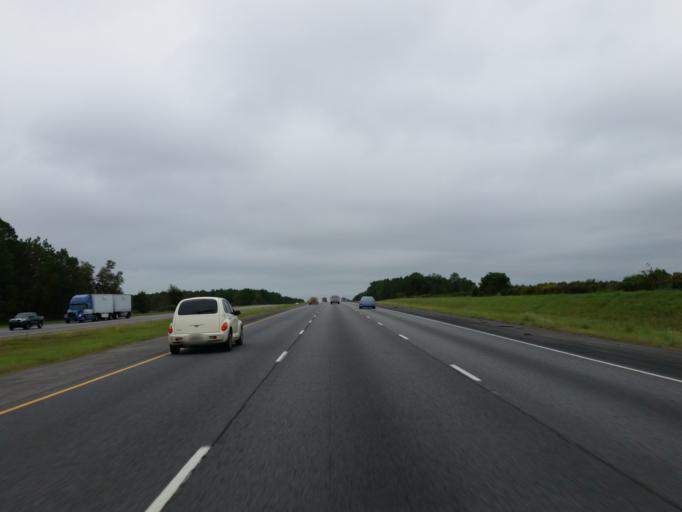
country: US
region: Georgia
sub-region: Crisp County
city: Cordele
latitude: 31.8851
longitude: -83.7296
